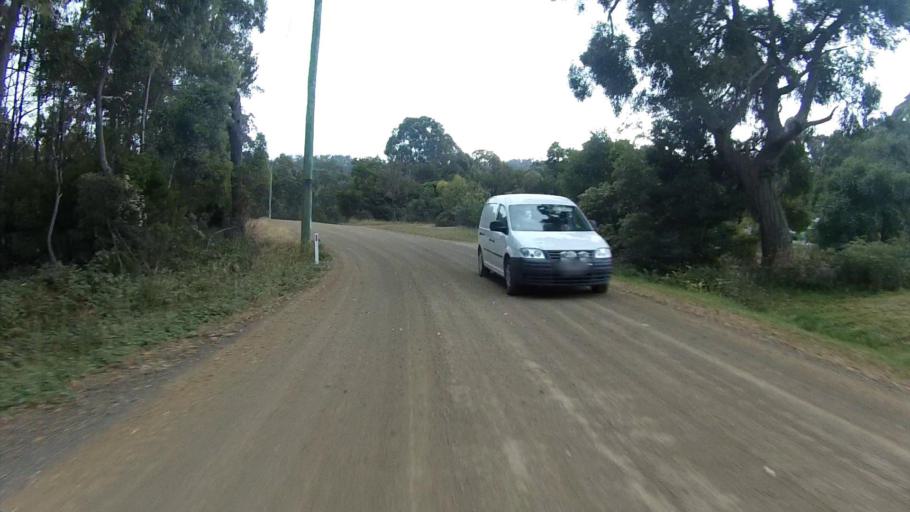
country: AU
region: Tasmania
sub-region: Huon Valley
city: Cygnet
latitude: -43.2277
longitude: 147.0961
